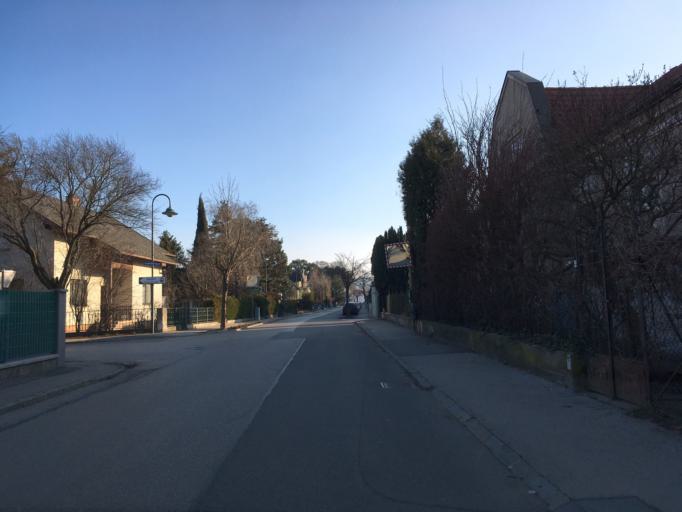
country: AT
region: Lower Austria
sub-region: Politischer Bezirk Tulln
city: Konigstetten
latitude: 48.3307
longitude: 16.1211
